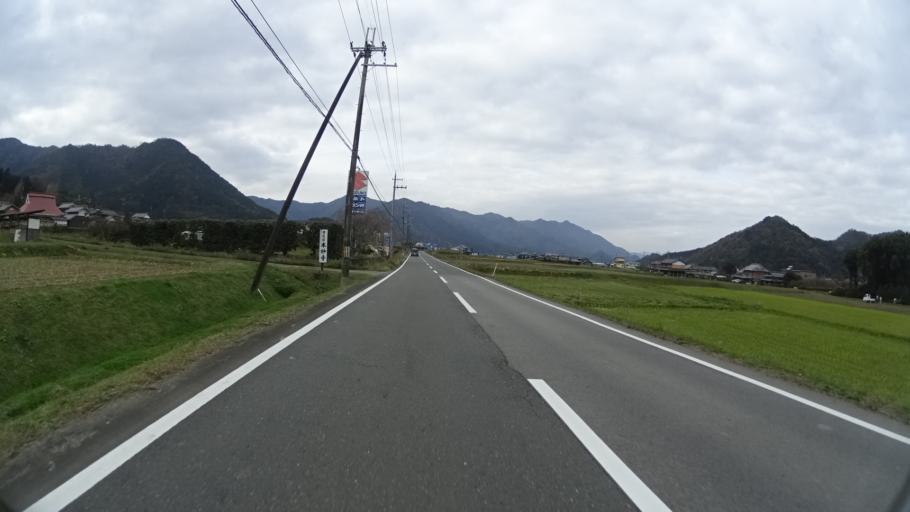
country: JP
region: Hyogo
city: Sasayama
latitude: 35.1437
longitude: 135.1459
